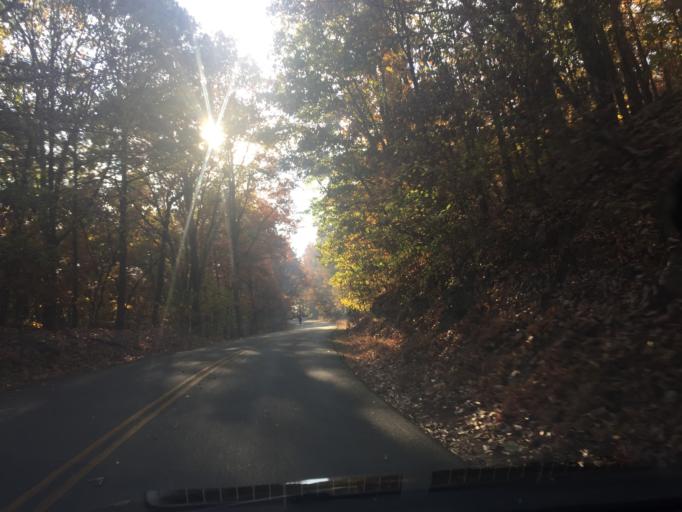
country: US
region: Georgia
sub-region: Cobb County
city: Marietta
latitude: 33.9823
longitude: -84.5741
